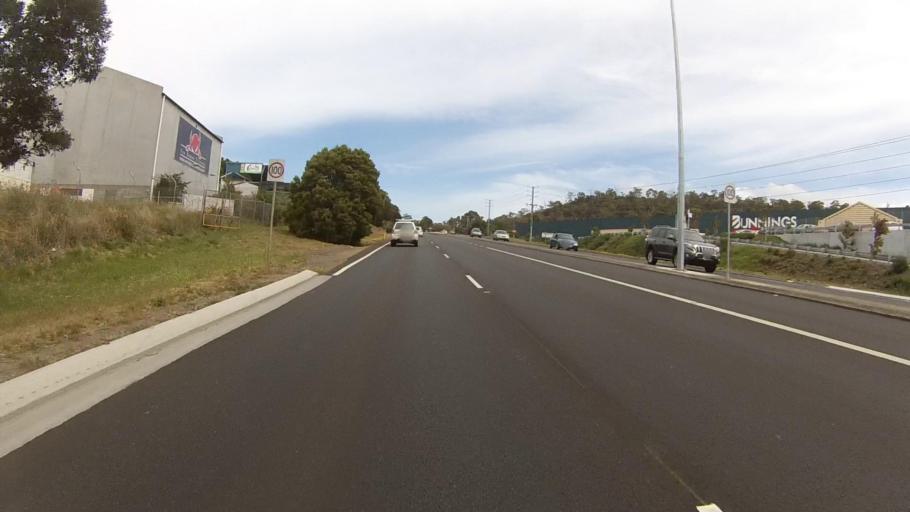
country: AU
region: Tasmania
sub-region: Clarence
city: Warrane
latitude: -42.8609
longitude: 147.3939
